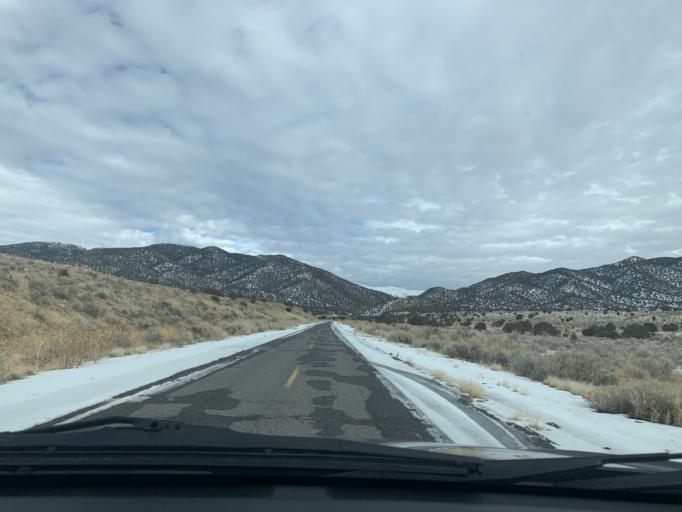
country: US
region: Utah
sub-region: Tooele County
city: Tooele
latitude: 40.3003
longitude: -112.2695
